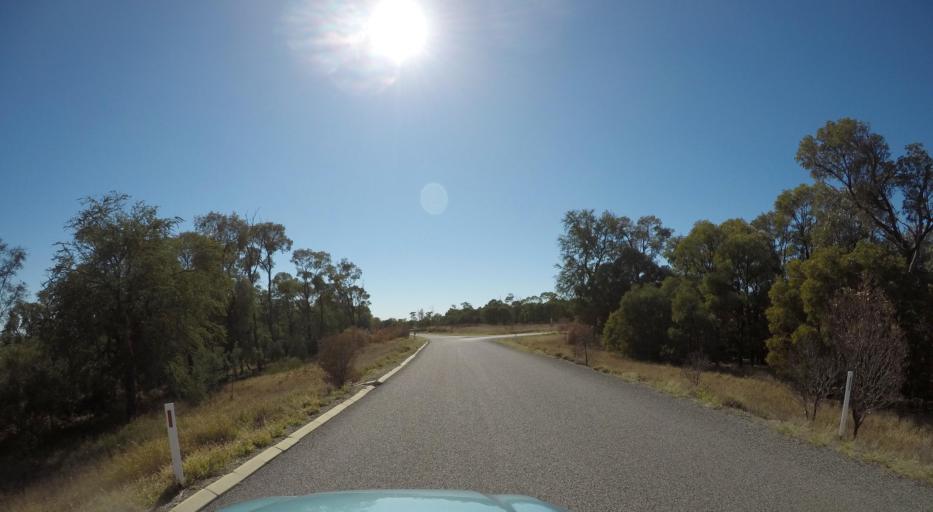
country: AU
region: Queensland
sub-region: Banana
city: Taroom
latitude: -25.7881
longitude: 149.6939
